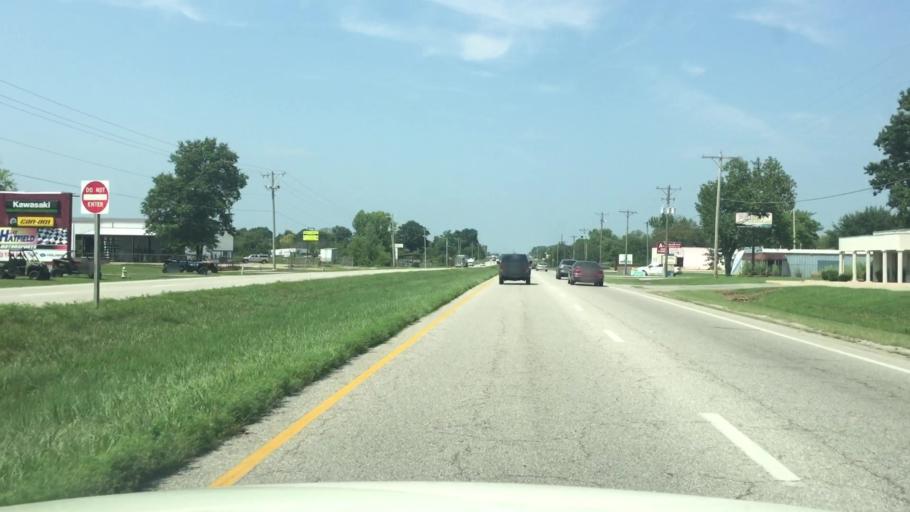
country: US
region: Kansas
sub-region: Crawford County
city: Frontenac
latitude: 37.4600
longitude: -94.7051
